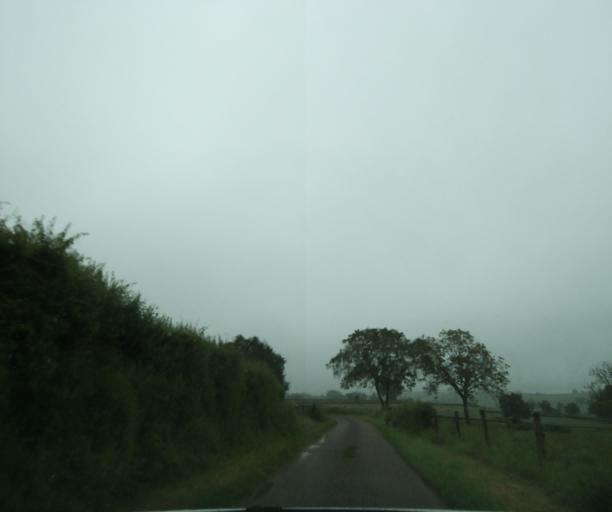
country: FR
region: Bourgogne
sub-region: Departement de Saone-et-Loire
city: Charolles
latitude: 46.3964
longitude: 4.2173
